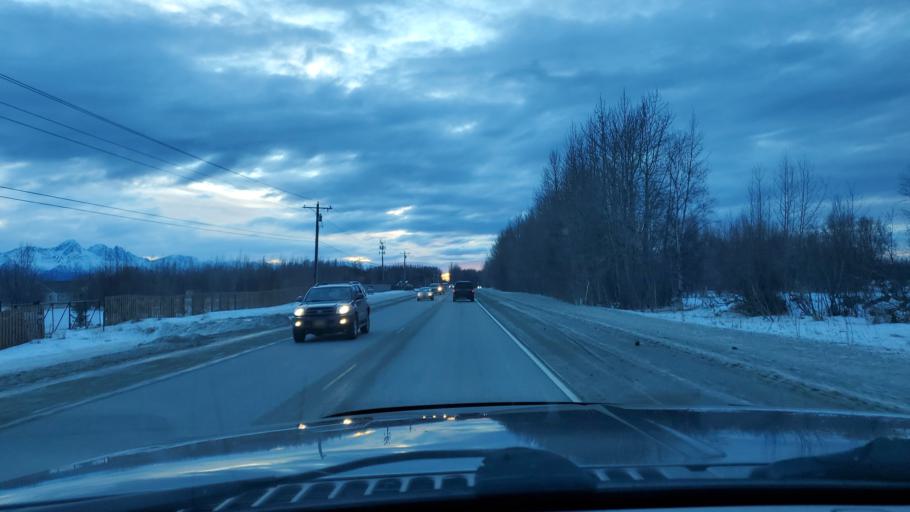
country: US
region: Alaska
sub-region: Matanuska-Susitna Borough
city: Farm Loop
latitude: 61.6611
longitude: -149.0918
